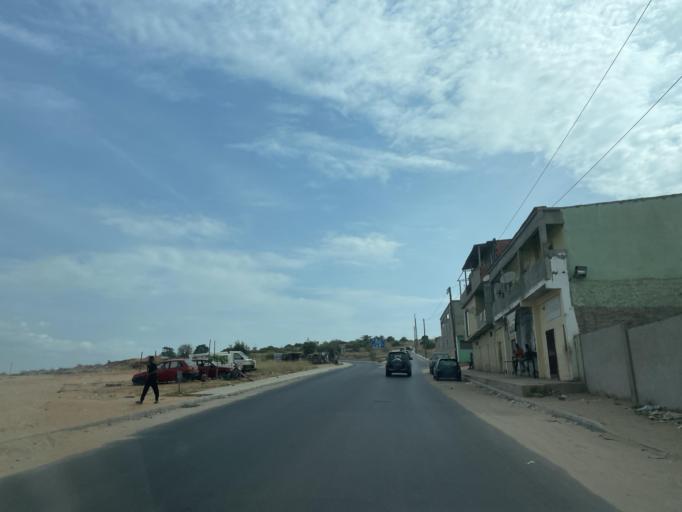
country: AO
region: Luanda
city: Luanda
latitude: -8.9377
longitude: 13.1963
